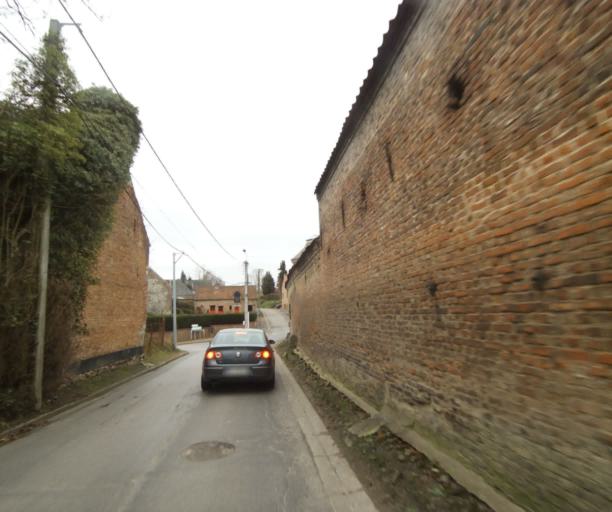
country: FR
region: Nord-Pas-de-Calais
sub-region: Departement du Nord
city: Sebourg
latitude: 50.3517
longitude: 3.6448
